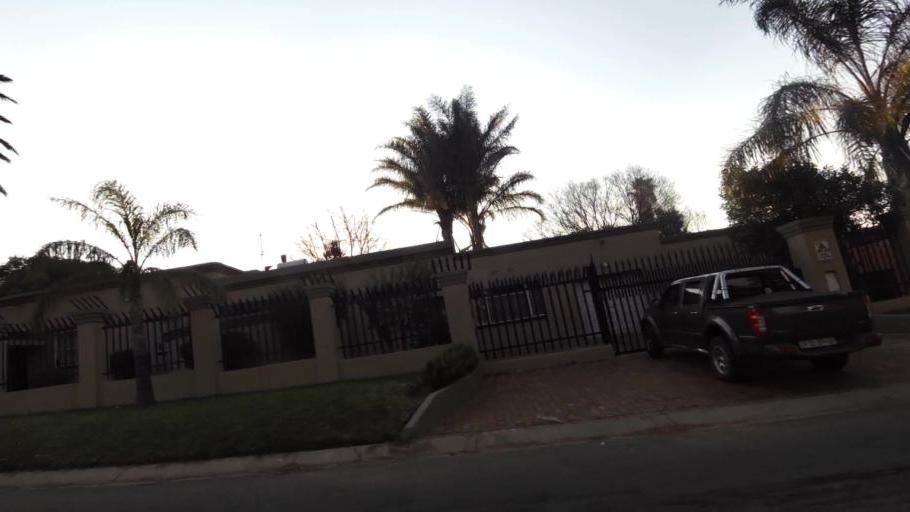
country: ZA
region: Gauteng
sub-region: City of Johannesburg Metropolitan Municipality
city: Roodepoort
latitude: -26.1693
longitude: 27.9598
